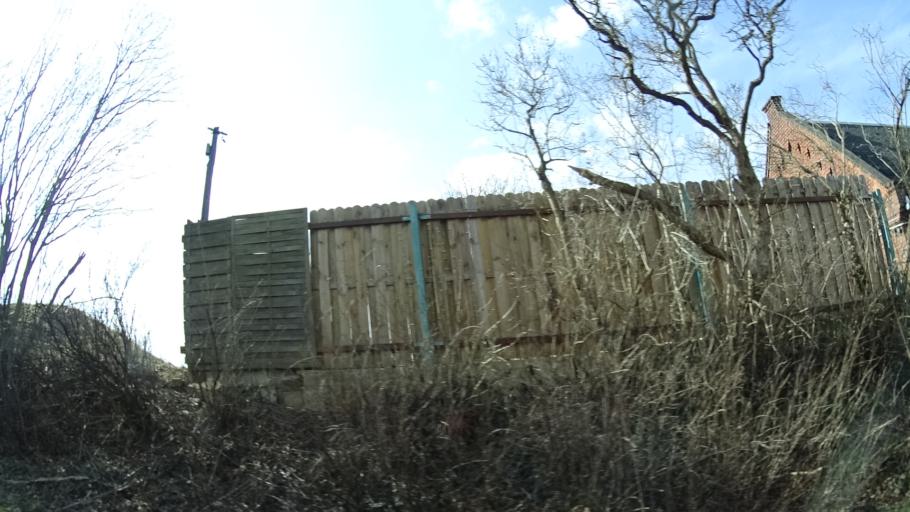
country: DE
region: Saxony-Anhalt
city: Prittitz
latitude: 51.1474
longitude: 11.9295
